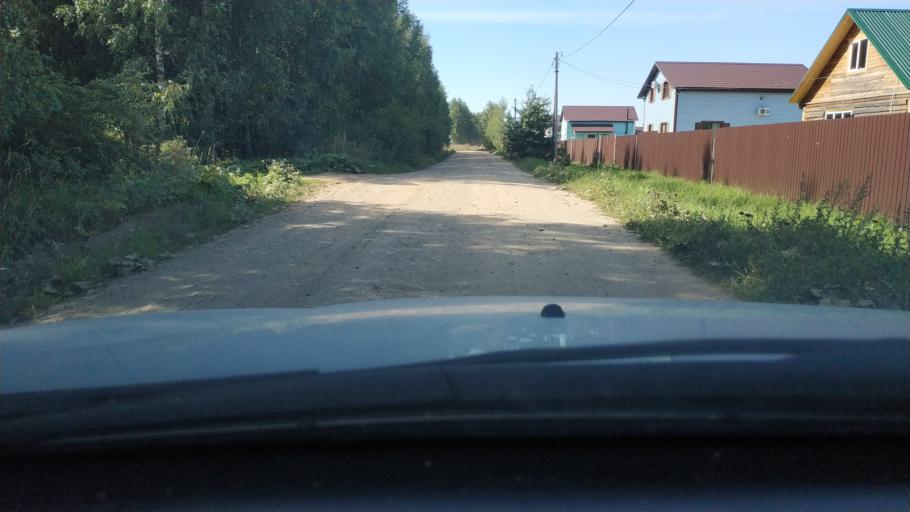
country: RU
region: Kostroma
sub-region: Kostromskoy Rayon
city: Kostroma
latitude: 57.7772
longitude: 40.7421
